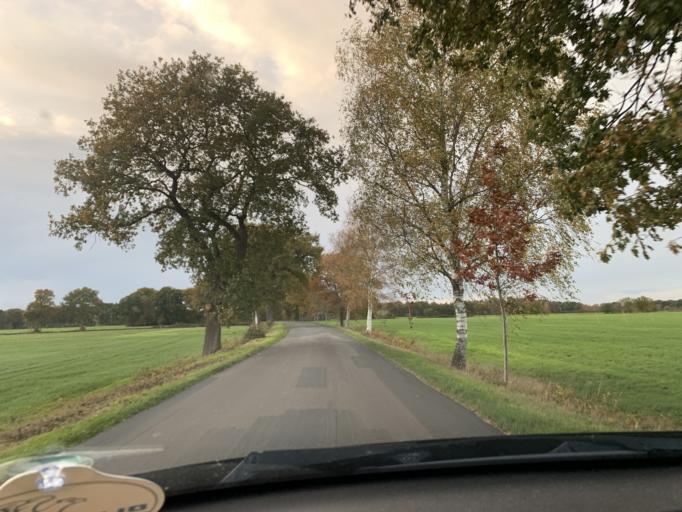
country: DE
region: Lower Saxony
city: Wiefelstede
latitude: 53.2645
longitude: 8.0914
